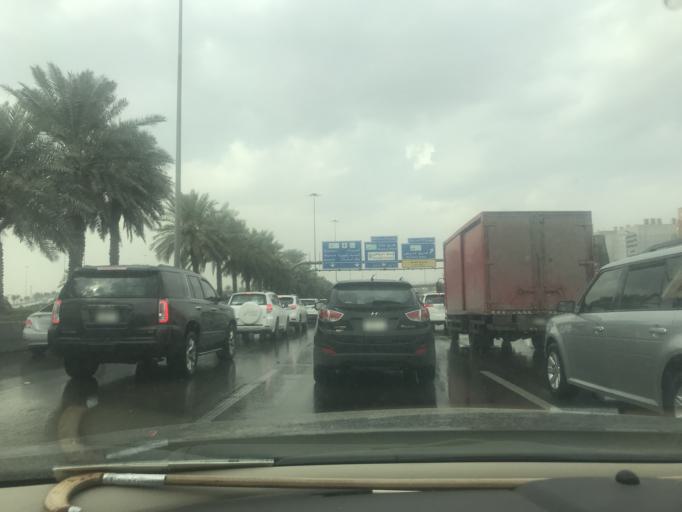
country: SA
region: Ar Riyad
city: Riyadh
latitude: 24.7113
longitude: 46.7642
